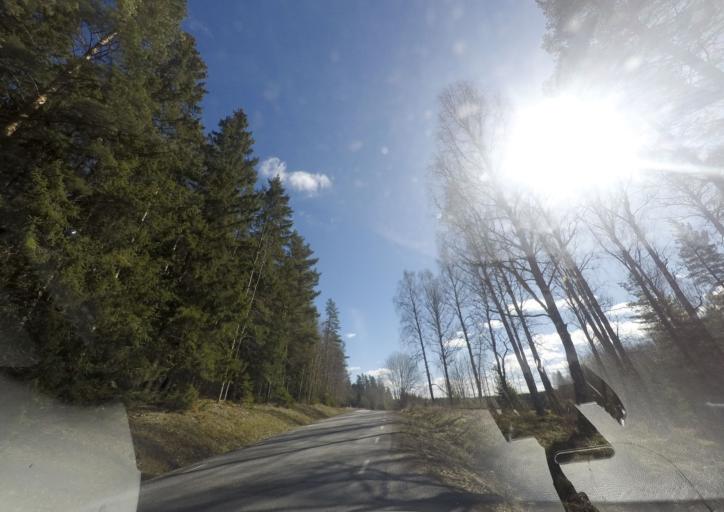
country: SE
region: Soedermanland
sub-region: Katrineholms Kommun
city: Katrineholm
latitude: 58.8943
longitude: 16.3477
